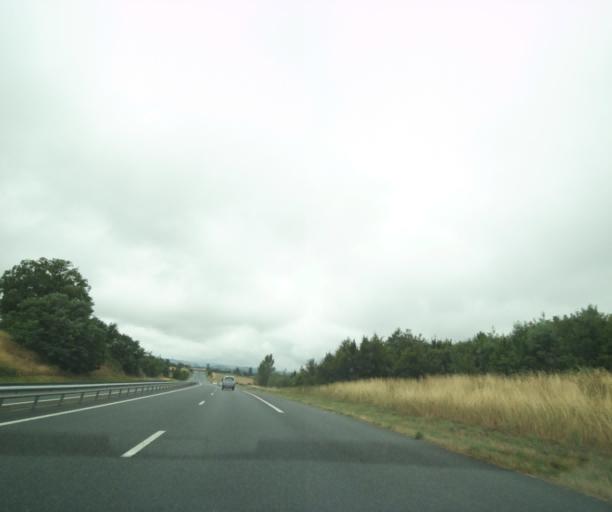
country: FR
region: Midi-Pyrenees
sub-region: Departement de l'Aveyron
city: Luc-la-Primaube
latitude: 44.3086
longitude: 2.5383
